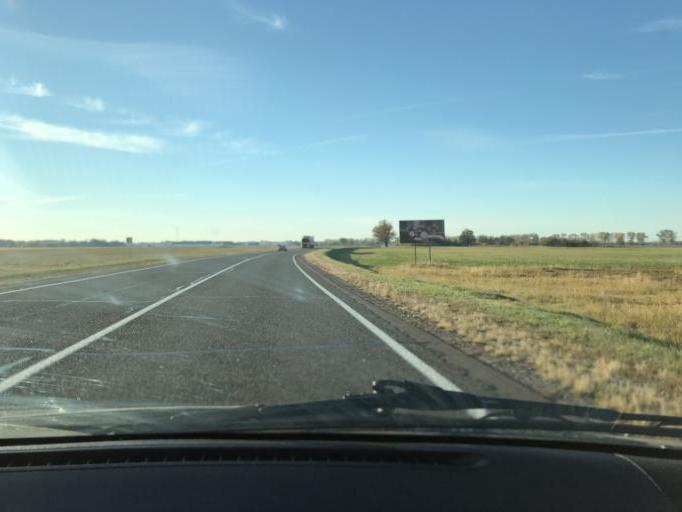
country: BY
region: Brest
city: Horad Kobryn
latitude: 52.2100
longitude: 24.4685
